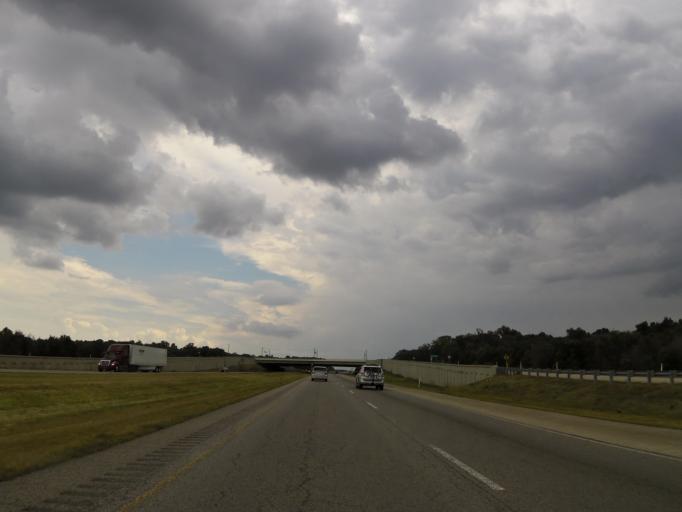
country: US
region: Tennessee
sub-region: Wilson County
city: Rural Hill
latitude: 36.0431
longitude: -86.4298
